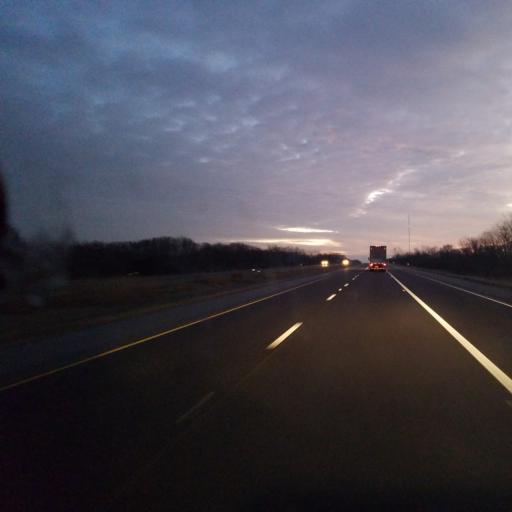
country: US
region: Illinois
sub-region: Tazewell County
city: Marquette Heights
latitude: 40.6299
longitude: -89.5908
